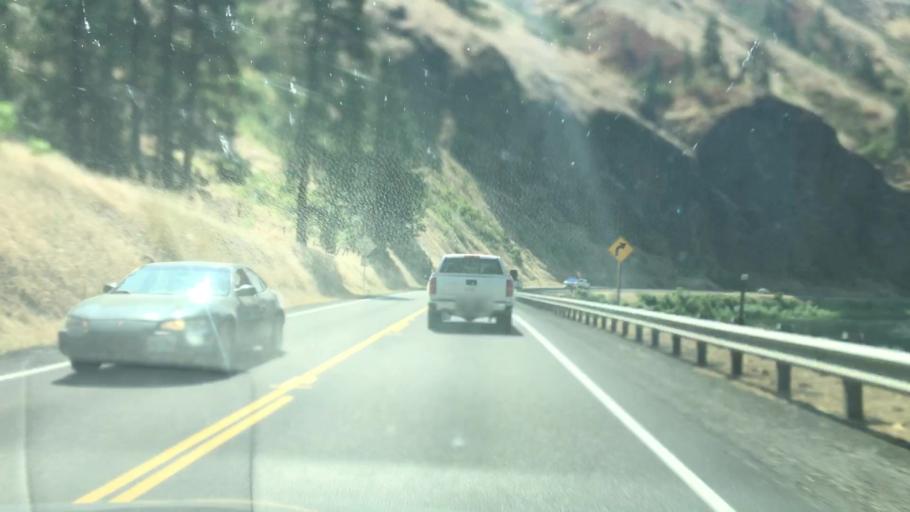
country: US
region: Idaho
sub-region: Nez Perce County
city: Lapwai
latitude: 46.4959
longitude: -116.7254
